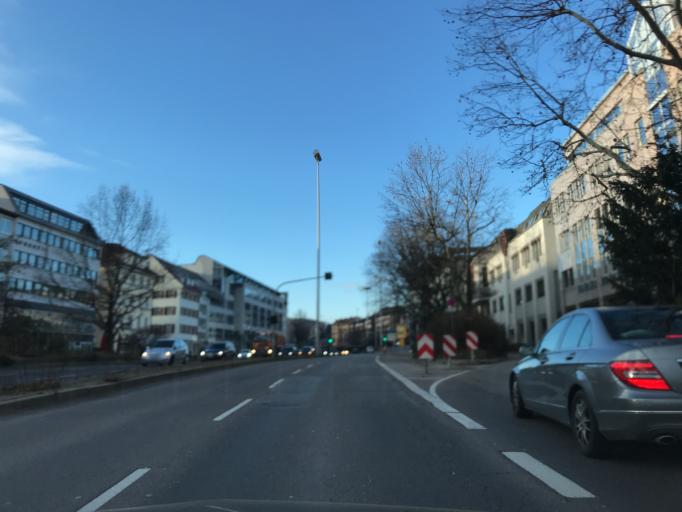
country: DE
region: Baden-Wuerttemberg
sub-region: Regierungsbezirk Stuttgart
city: Stuttgart
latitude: 48.7711
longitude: 9.1769
